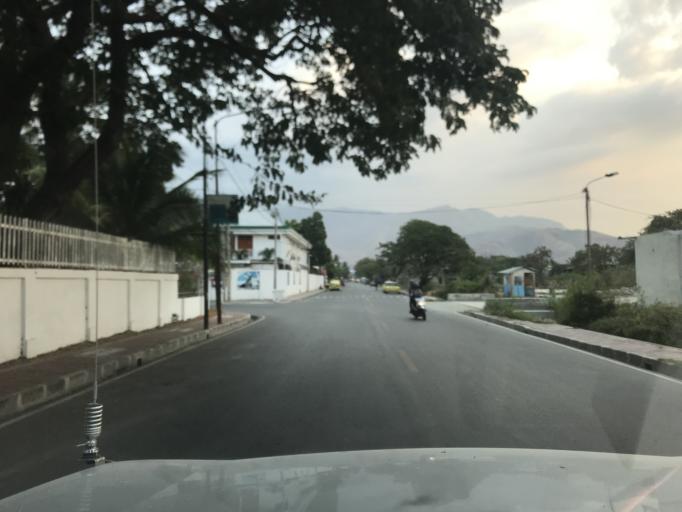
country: TL
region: Dili
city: Dili
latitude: -8.5494
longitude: 125.5651
